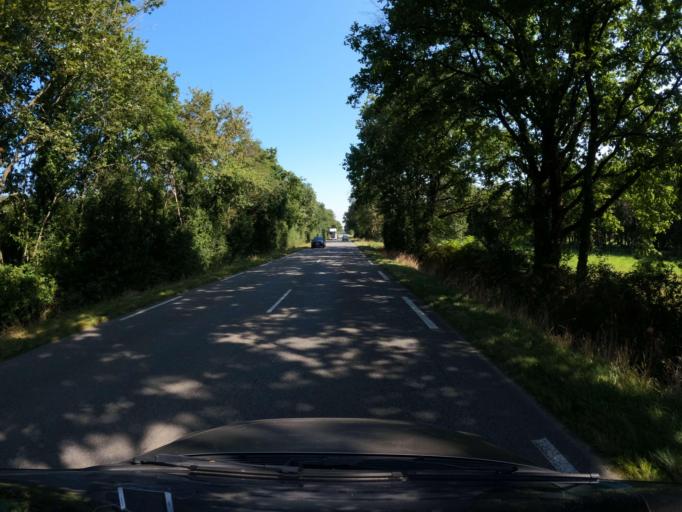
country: FR
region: Pays de la Loire
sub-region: Departement de la Loire-Atlantique
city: Pont-Saint-Martin
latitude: 47.0906
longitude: -1.5587
